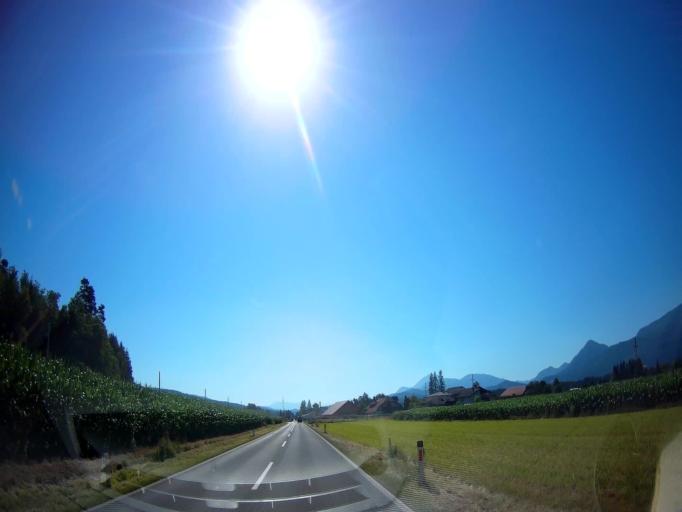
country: AT
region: Carinthia
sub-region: Politischer Bezirk Volkermarkt
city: Feistritz ob Bleiburg
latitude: 46.5773
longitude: 14.7684
